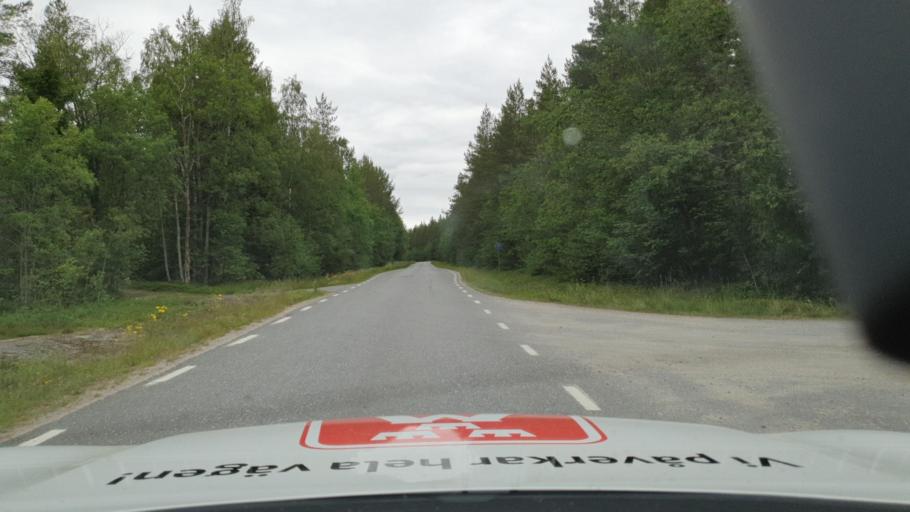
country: SE
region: Vaesterbotten
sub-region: Nordmalings Kommun
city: Nordmaling
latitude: 63.4762
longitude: 19.4597
